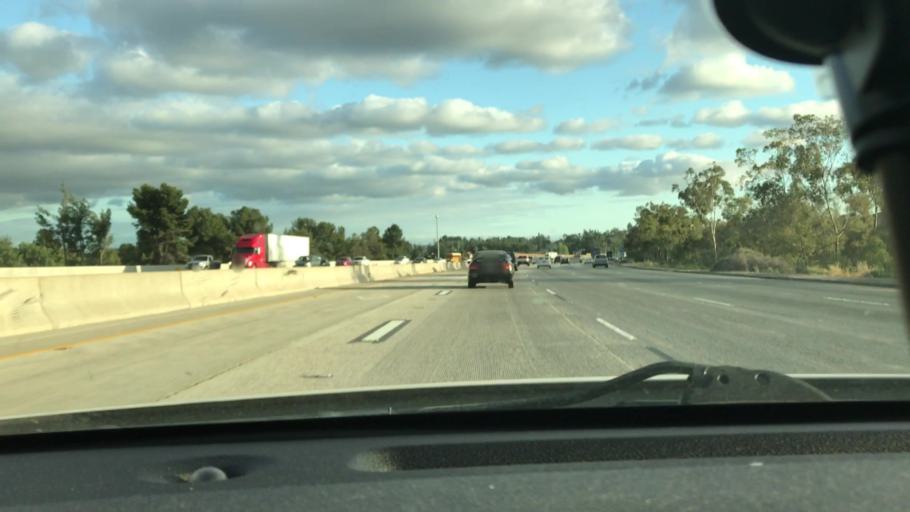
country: US
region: California
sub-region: Orange County
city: Brea
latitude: 33.9209
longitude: -117.8803
